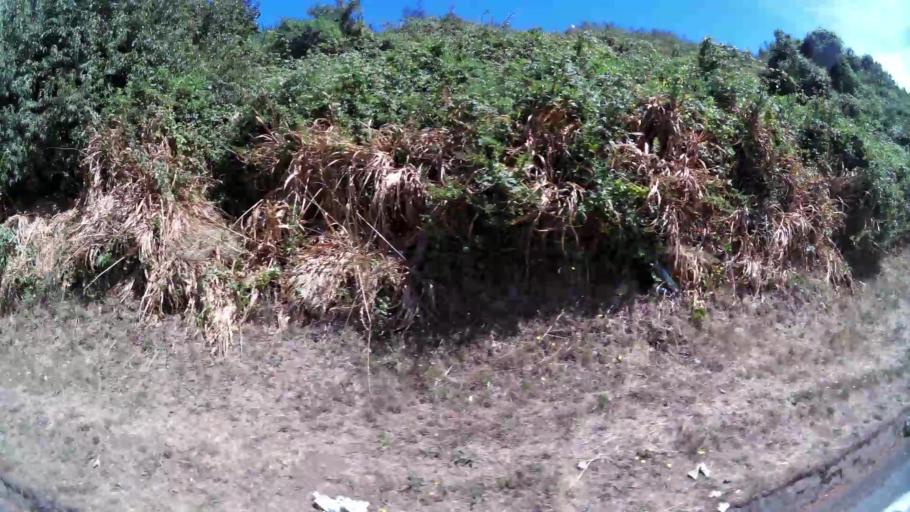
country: CL
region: Biobio
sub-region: Provincia de Concepcion
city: Talcahuano
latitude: -36.7132
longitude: -73.1262
